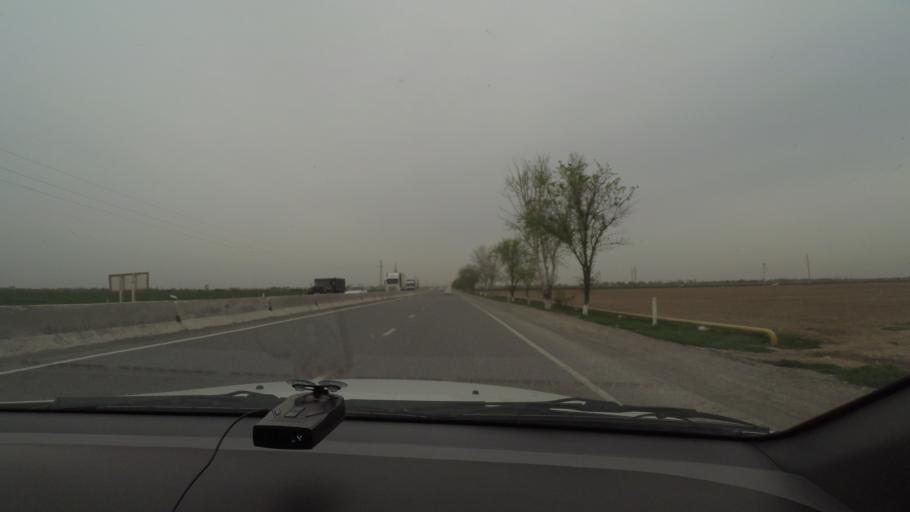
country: KZ
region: Ongtustik Qazaqstan
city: Myrzakent
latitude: 40.5575
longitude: 68.3888
